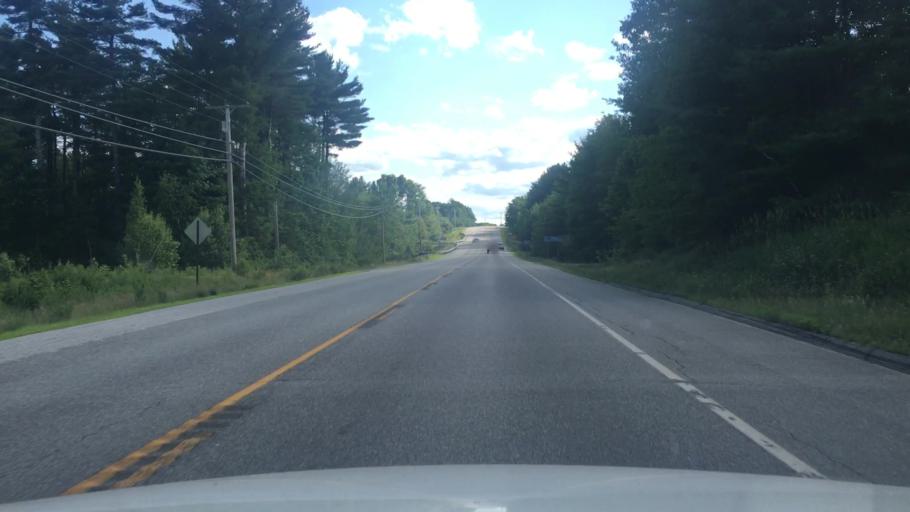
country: US
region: Maine
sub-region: Androscoggin County
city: Livermore Falls
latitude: 44.4471
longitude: -70.2006
